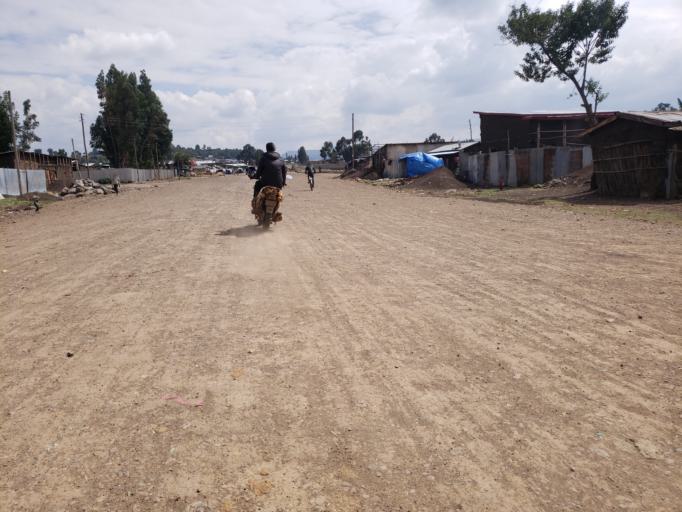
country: ET
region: Oromiya
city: Dodola
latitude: 7.0024
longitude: 39.3917
